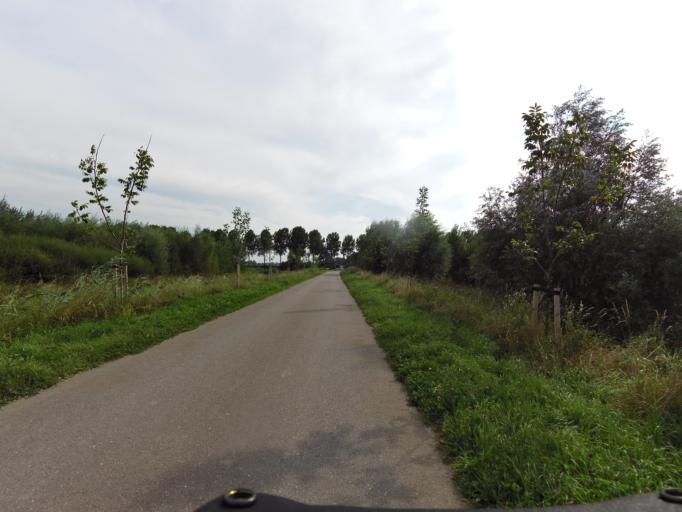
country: NL
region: South Holland
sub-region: Gemeente Zwijndrecht
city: Zwijndrecht
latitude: 51.7932
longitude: 4.5975
